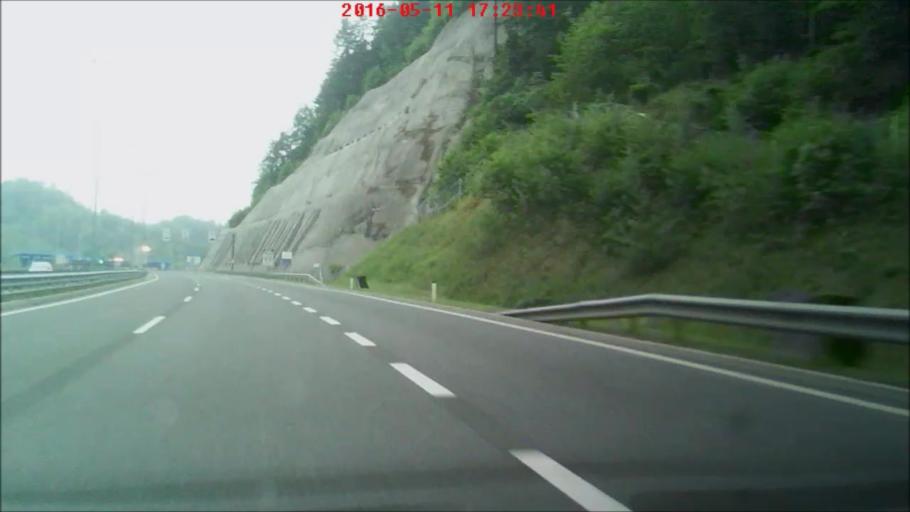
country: SI
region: Zetale
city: Zetale
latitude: 46.2723
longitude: 15.8670
